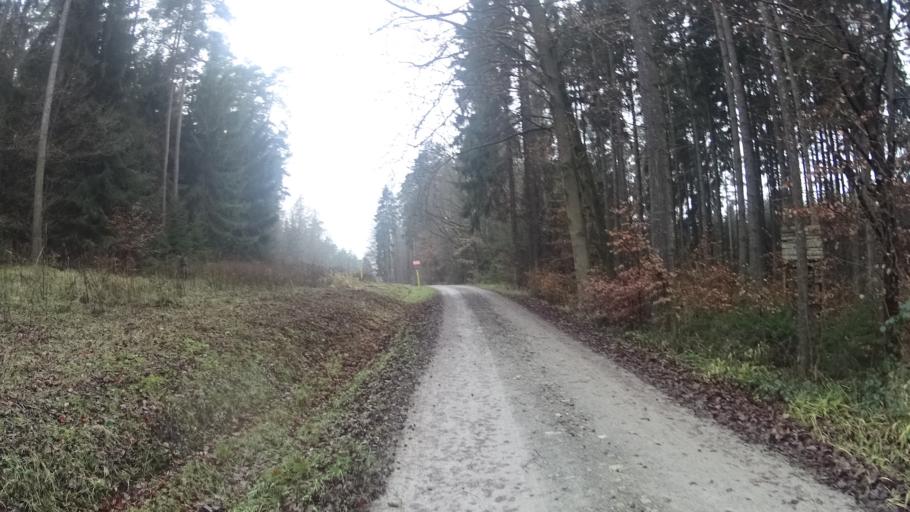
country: DE
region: Thuringia
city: Tissa
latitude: 50.8681
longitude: 11.7466
